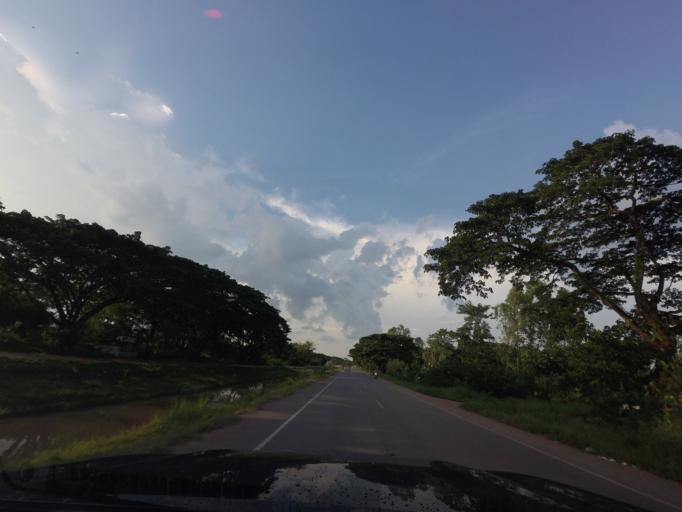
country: TH
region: Khon Kaen
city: Khon Kaen
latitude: 16.4153
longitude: 102.8619
